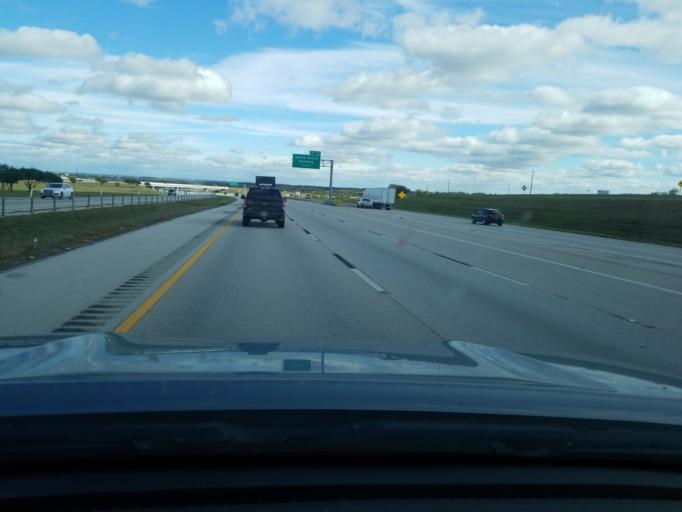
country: US
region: Texas
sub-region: Parker County
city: Aledo
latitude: 32.7239
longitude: -97.5745
